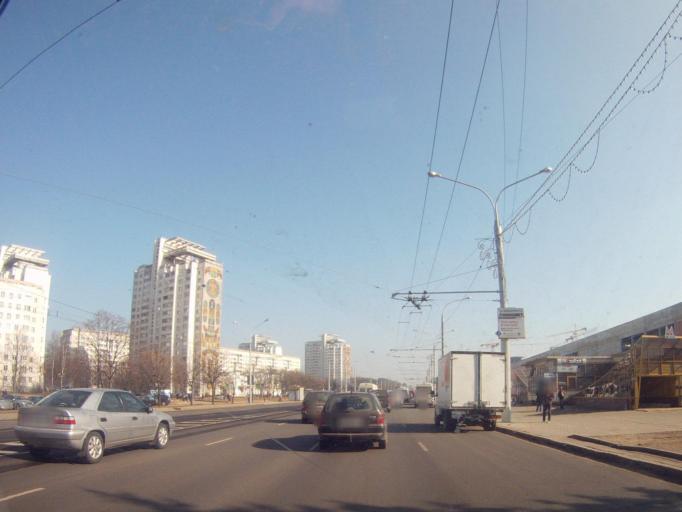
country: BY
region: Minsk
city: Borovlyany
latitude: 53.9339
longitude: 27.6494
